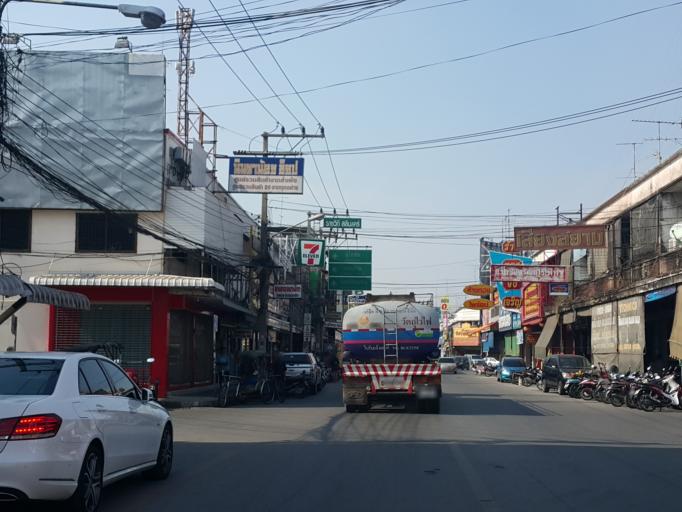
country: TH
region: Phitsanulok
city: Phitsanulok
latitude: 16.8138
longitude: 100.2646
